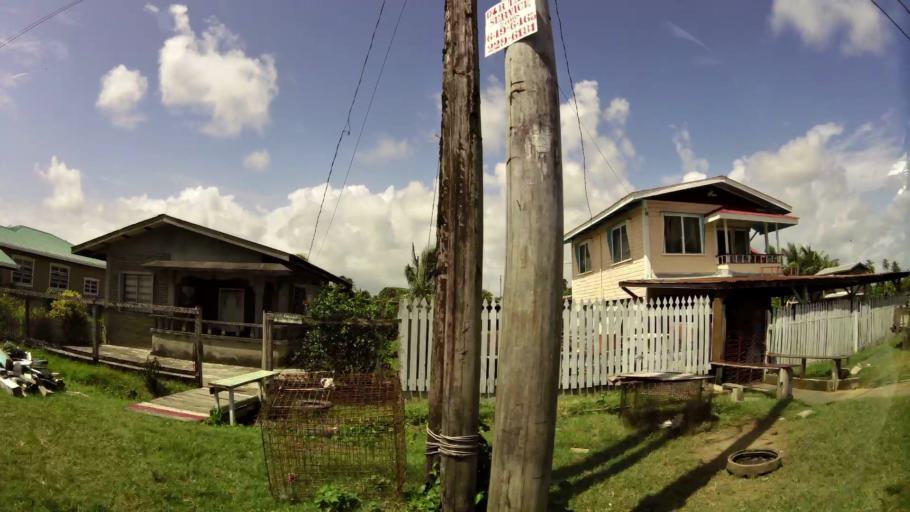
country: GY
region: Demerara-Mahaica
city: Mahaica Village
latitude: 6.7689
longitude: -58.0075
